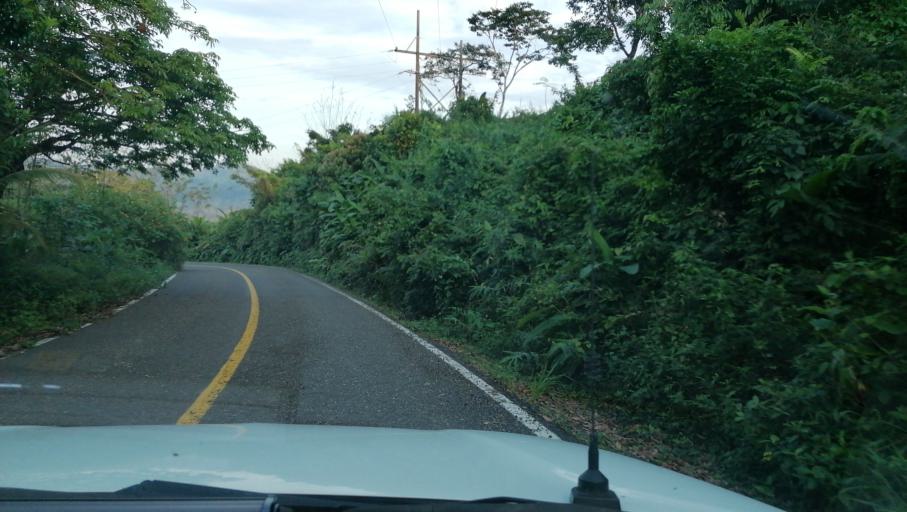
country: MX
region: Chiapas
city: Pichucalco
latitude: 17.5060
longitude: -93.2142
